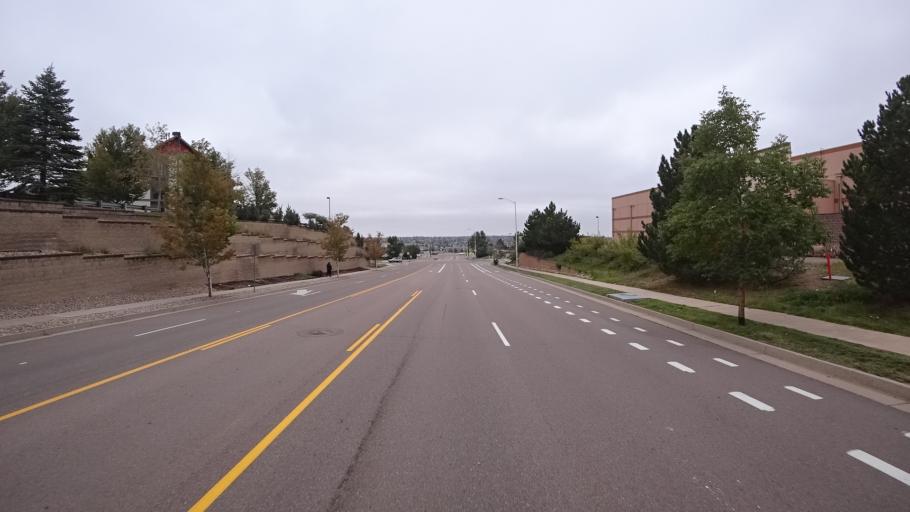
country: US
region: Colorado
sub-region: El Paso County
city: Cimarron Hills
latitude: 38.8964
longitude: -104.7167
